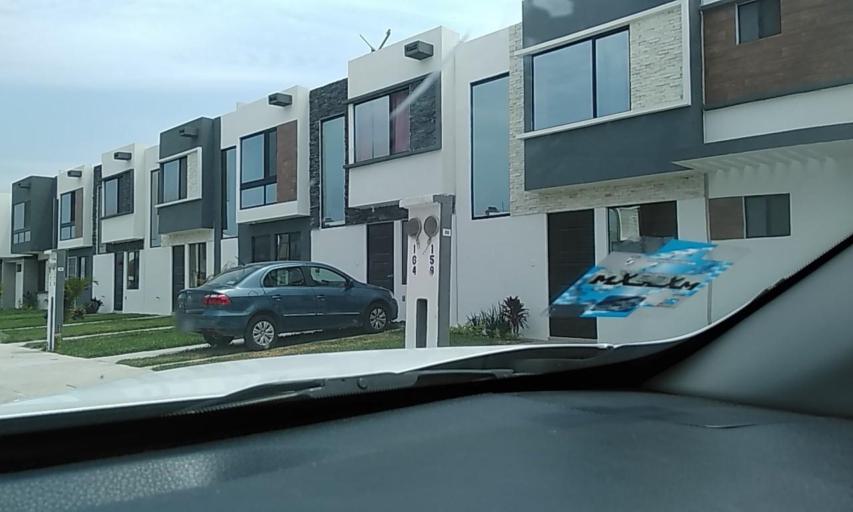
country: MX
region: Veracruz
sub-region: Veracruz
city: Las Amapolas
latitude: 19.1493
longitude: -96.2168
